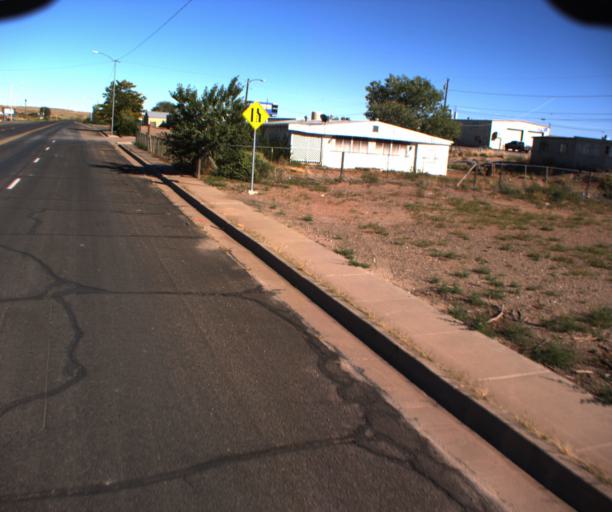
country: US
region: Arizona
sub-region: Navajo County
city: Joseph City
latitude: 34.9559
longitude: -110.3274
